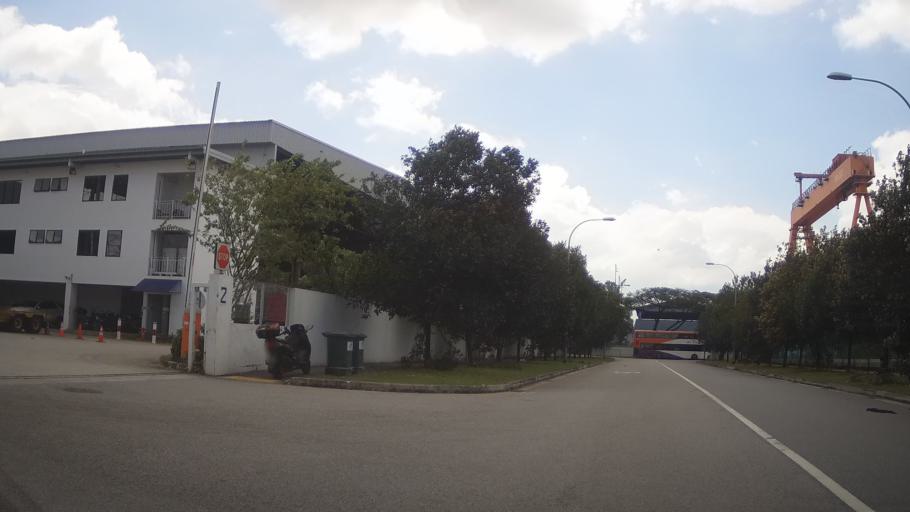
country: MY
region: Johor
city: Johor Bahru
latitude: 1.3089
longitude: 103.6490
